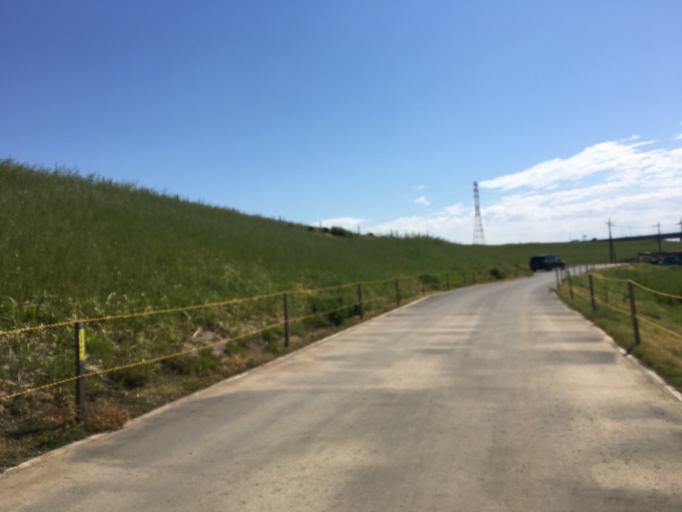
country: JP
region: Saitama
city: Asaka
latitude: 35.8104
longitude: 139.6194
